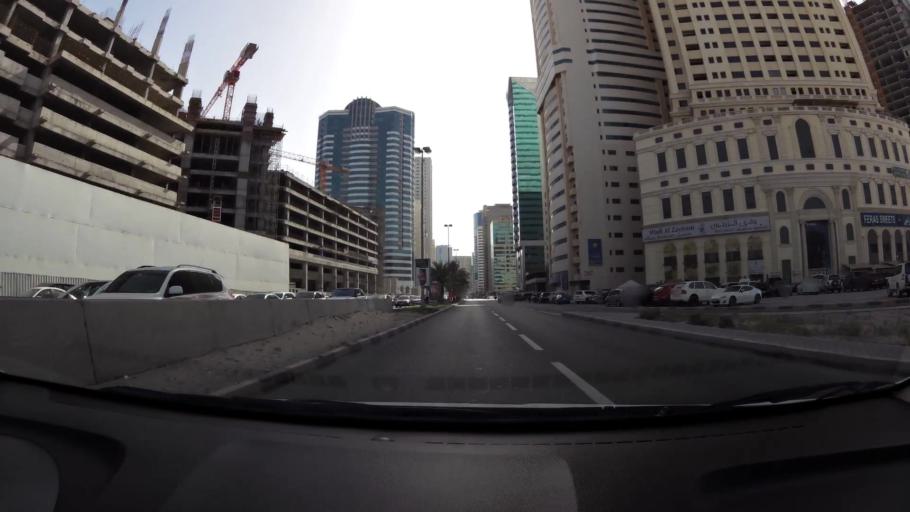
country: AE
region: Ash Shariqah
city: Sharjah
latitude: 25.3047
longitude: 55.3625
